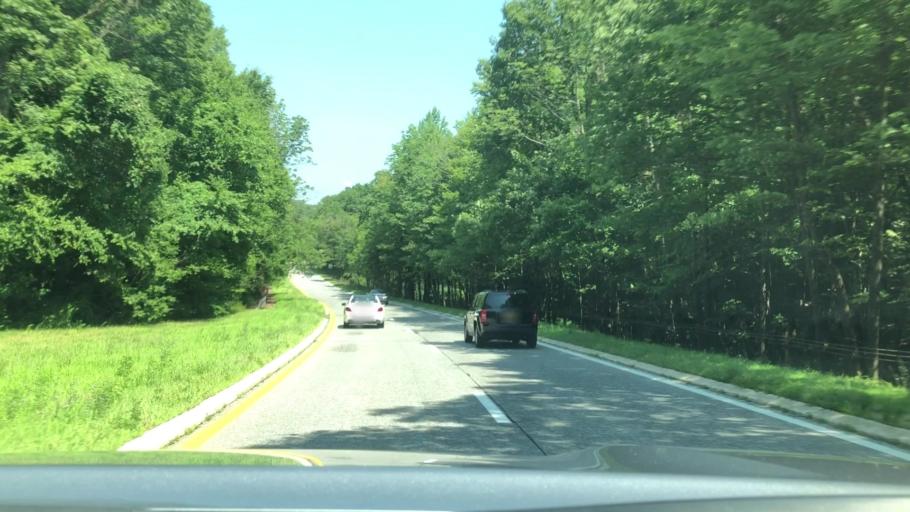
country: US
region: New York
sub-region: Rockland County
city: Stony Point
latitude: 41.2715
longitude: -74.0304
